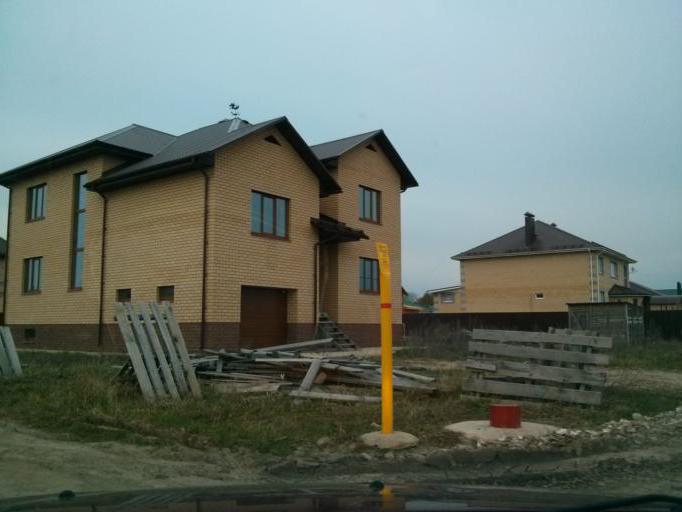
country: RU
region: Vladimir
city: Murom
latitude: 55.5442
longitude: 42.0657
